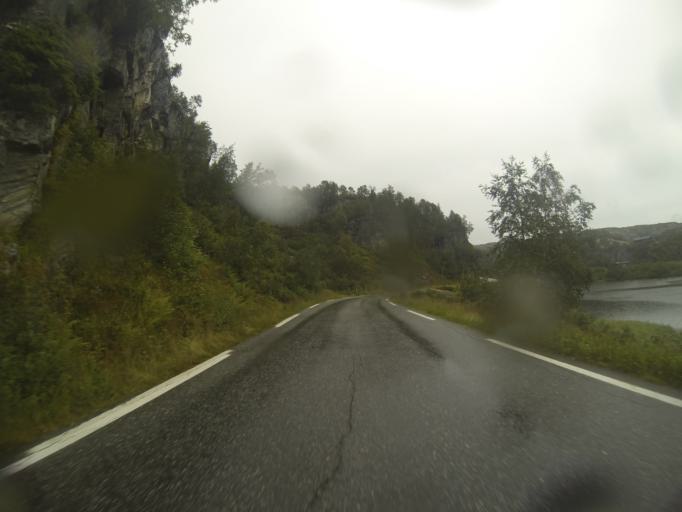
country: NO
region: Rogaland
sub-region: Sauda
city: Sauda
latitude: 59.7254
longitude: 6.5657
